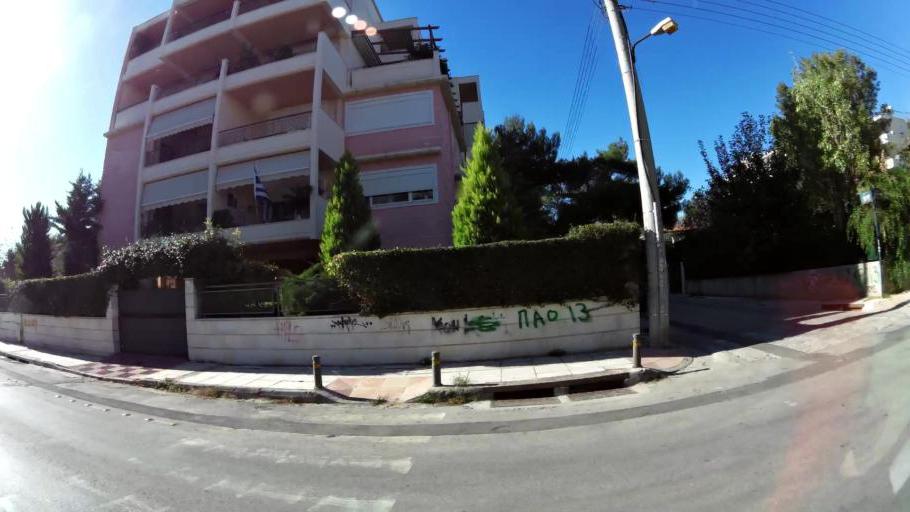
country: GR
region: Attica
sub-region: Nomarchia Athinas
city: Vrilissia
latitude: 38.0303
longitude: 23.8342
